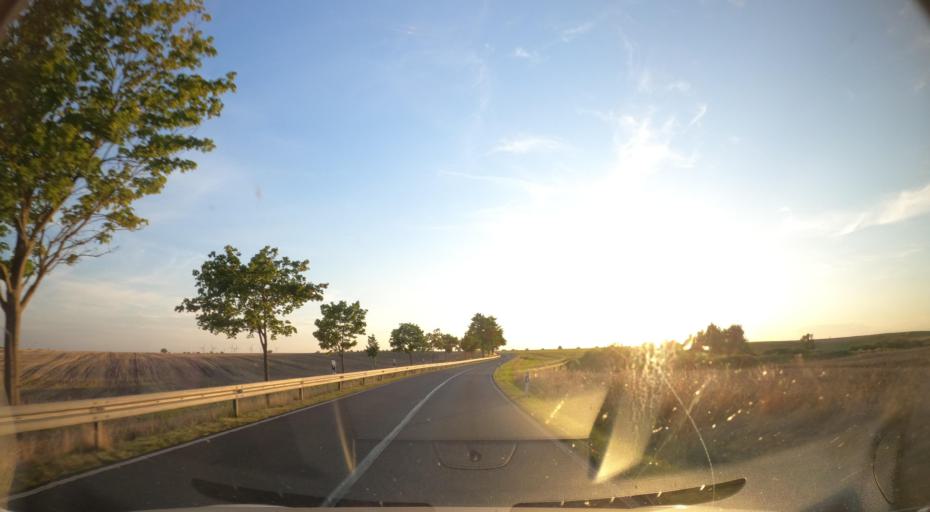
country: DE
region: Mecklenburg-Vorpommern
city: Pasewalk
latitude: 53.4962
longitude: 13.9281
